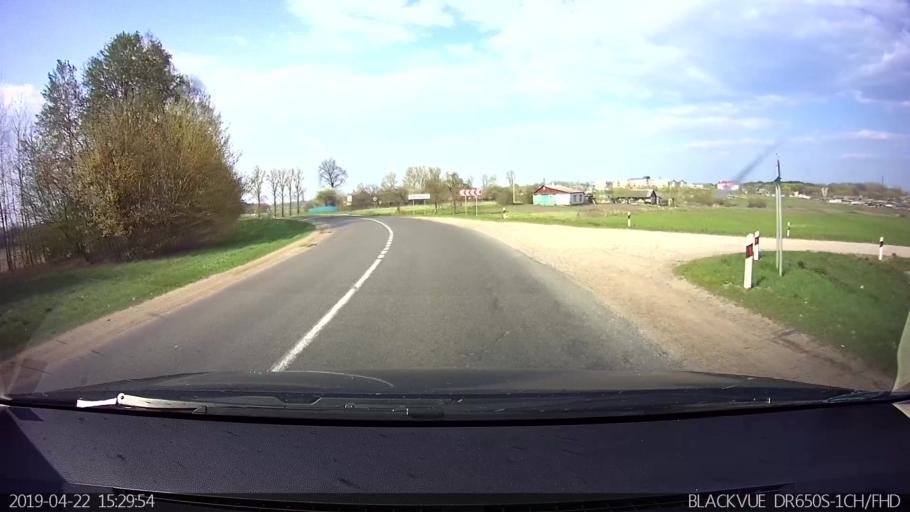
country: BY
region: Brest
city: Vysokaye
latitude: 52.3933
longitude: 23.3757
